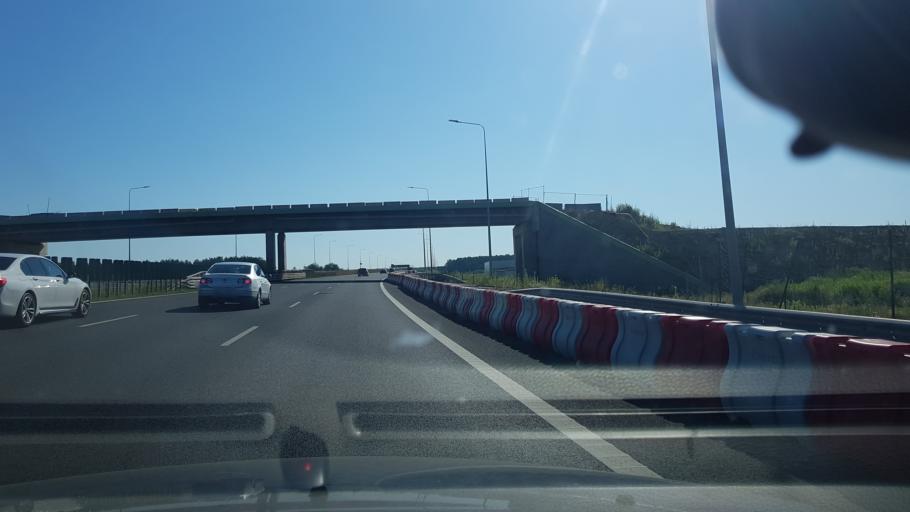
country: PL
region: Masovian Voivodeship
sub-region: Powiat wolominski
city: Slupno
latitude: 52.3521
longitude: 21.1647
